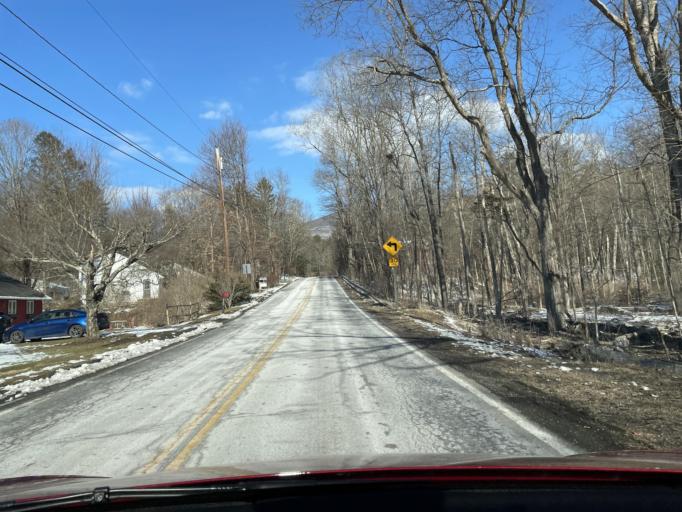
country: US
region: New York
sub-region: Ulster County
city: Zena
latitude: 42.0527
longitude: -74.0722
